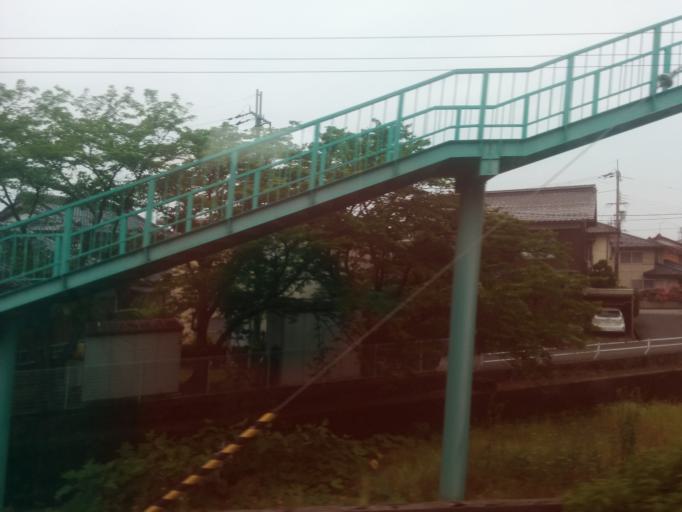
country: JP
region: Shiga Prefecture
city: Hikone
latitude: 35.2782
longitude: 136.2646
